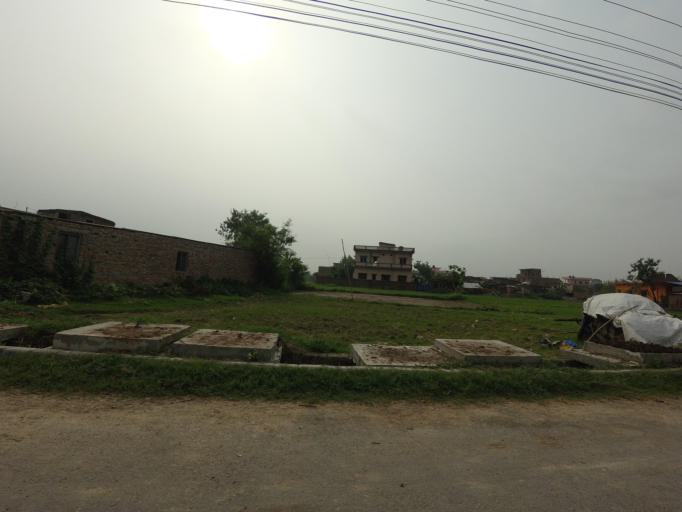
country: NP
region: Western Region
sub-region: Lumbini Zone
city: Bhairahawa
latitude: 27.4865
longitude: 83.4373
